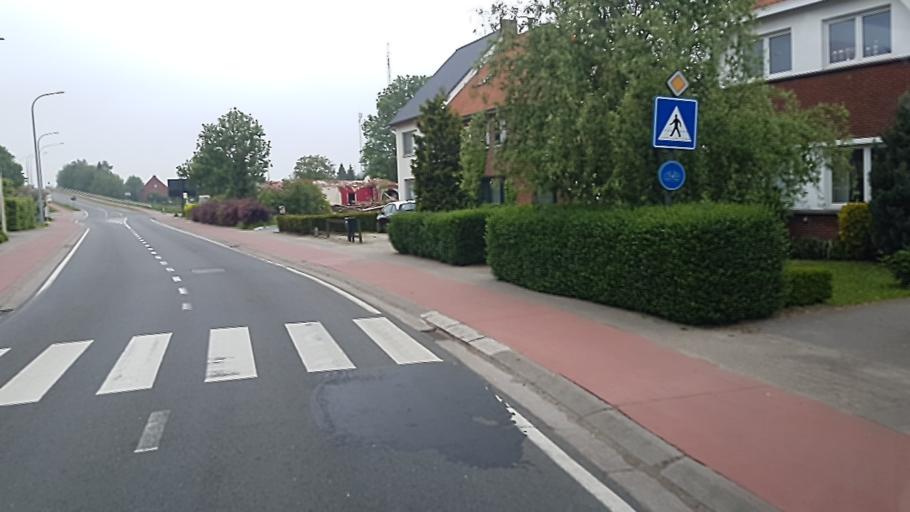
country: BE
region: Flanders
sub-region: Provincie Antwerpen
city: Brecht
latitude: 51.3516
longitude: 4.6357
